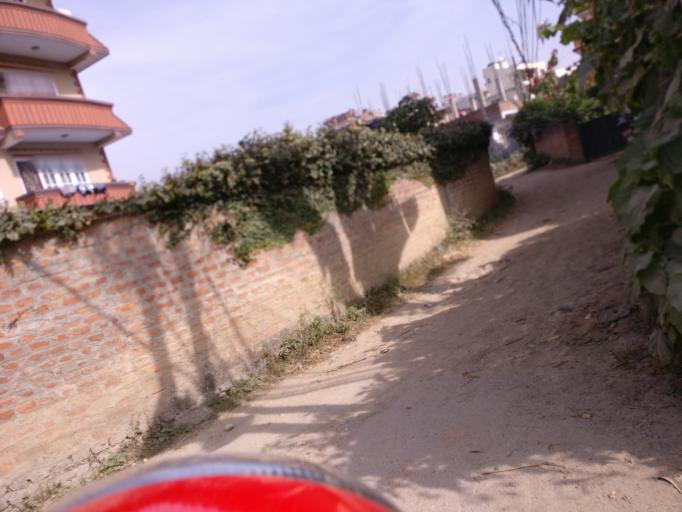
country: NP
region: Central Region
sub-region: Bagmati Zone
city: Patan
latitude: 27.6575
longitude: 85.3130
